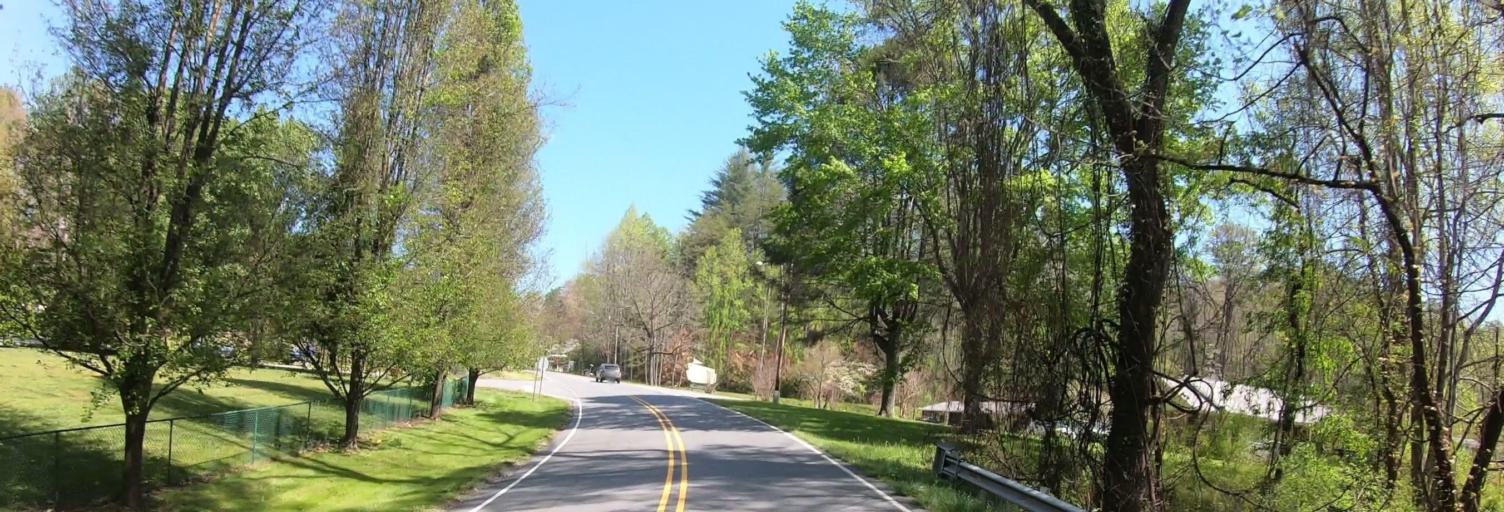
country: US
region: North Carolina
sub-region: Swain County
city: Cherokee
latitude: 35.4488
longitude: -83.3774
